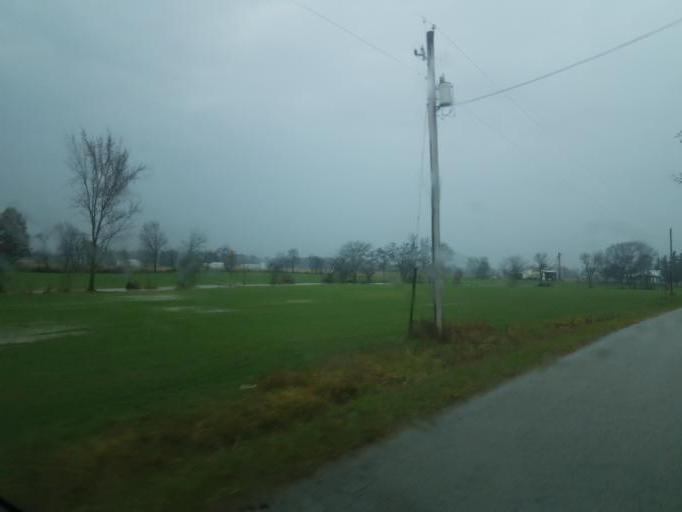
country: US
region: Ohio
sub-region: Morrow County
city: Cardington
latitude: 40.4542
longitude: -82.8715
